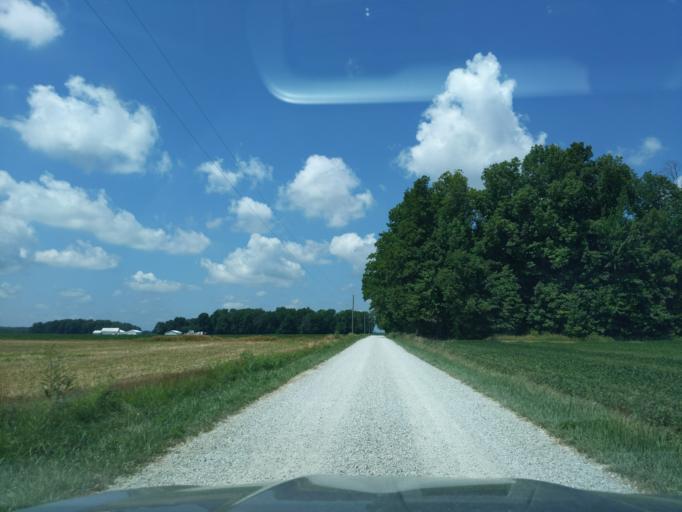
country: US
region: Indiana
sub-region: Ripley County
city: Osgood
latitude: 39.2210
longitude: -85.3558
